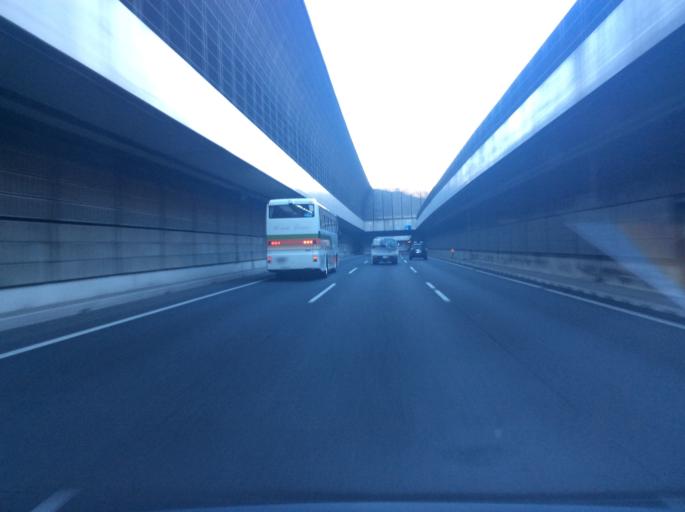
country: JP
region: Chiba
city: Nagareyama
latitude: 35.9001
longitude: 139.9258
